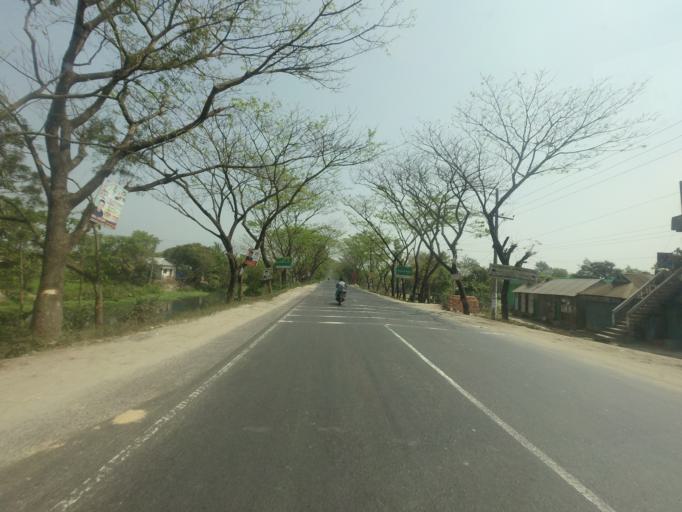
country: BD
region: Dhaka
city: Bhairab Bazar
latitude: 24.0457
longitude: 91.0755
